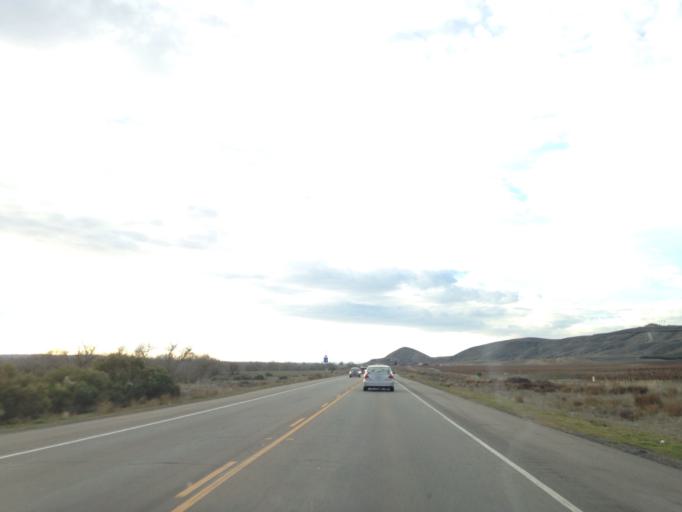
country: US
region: California
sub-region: San Luis Obispo County
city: Shandon
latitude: 35.6625
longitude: -120.3828
